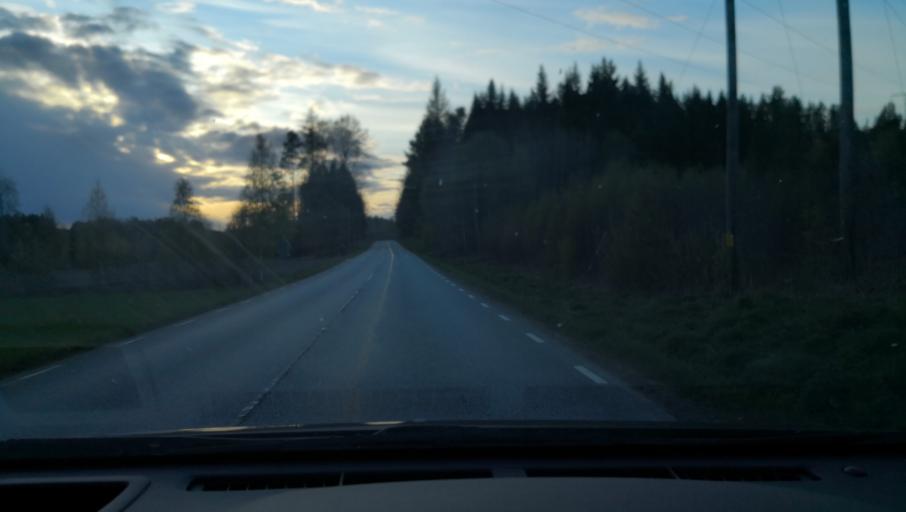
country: SE
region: OErebro
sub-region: Askersunds Kommun
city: Asbro
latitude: 58.9362
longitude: 15.0172
